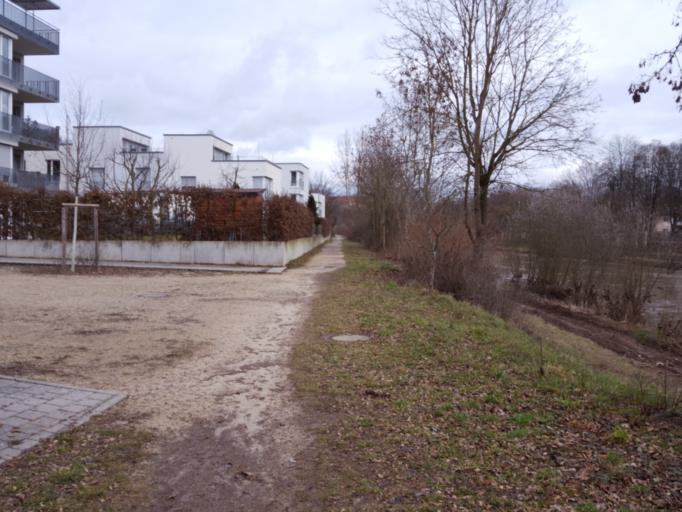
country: DE
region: Baden-Wuerttemberg
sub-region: Tuebingen Region
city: Tuebingen
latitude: 48.5114
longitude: 9.0377
